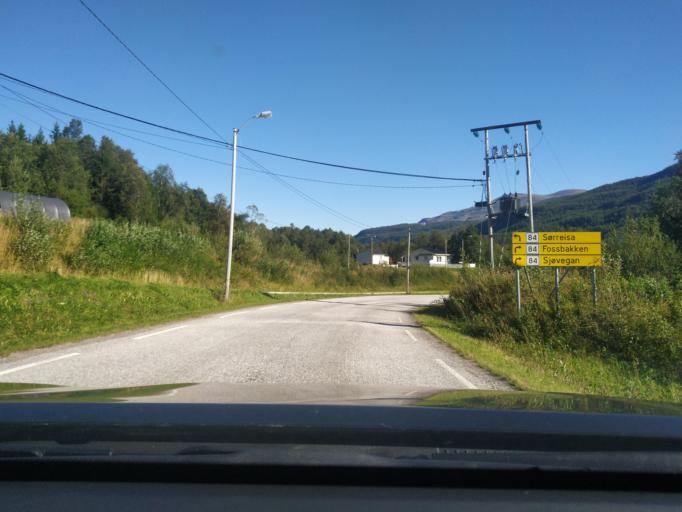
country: NO
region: Troms
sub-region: Salangen
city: Sjovegan
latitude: 68.9397
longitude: 17.7310
